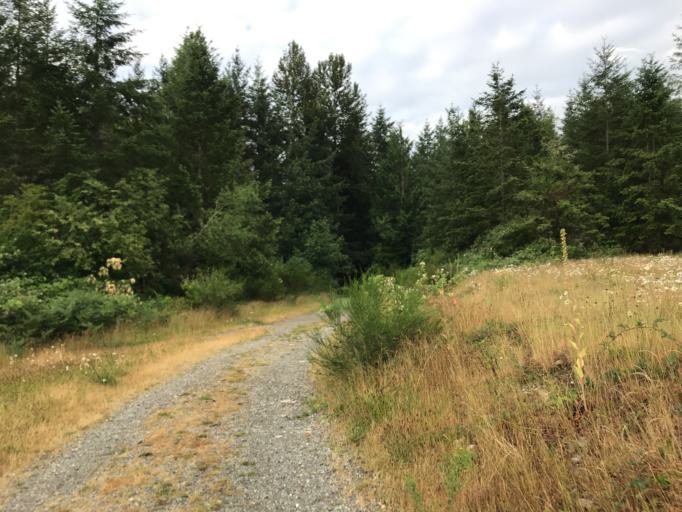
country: US
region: Washington
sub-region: King County
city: Ravensdale
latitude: 47.3491
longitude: -122.0080
